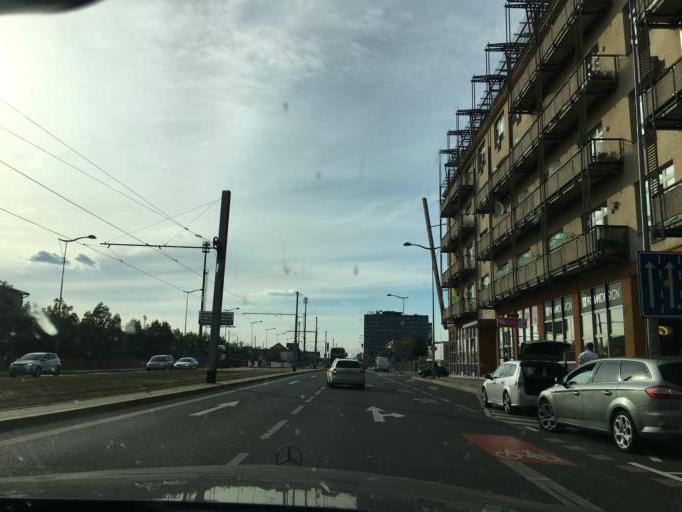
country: CZ
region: Praha
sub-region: Praha 9
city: Prosek
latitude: 50.1026
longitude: 14.4974
